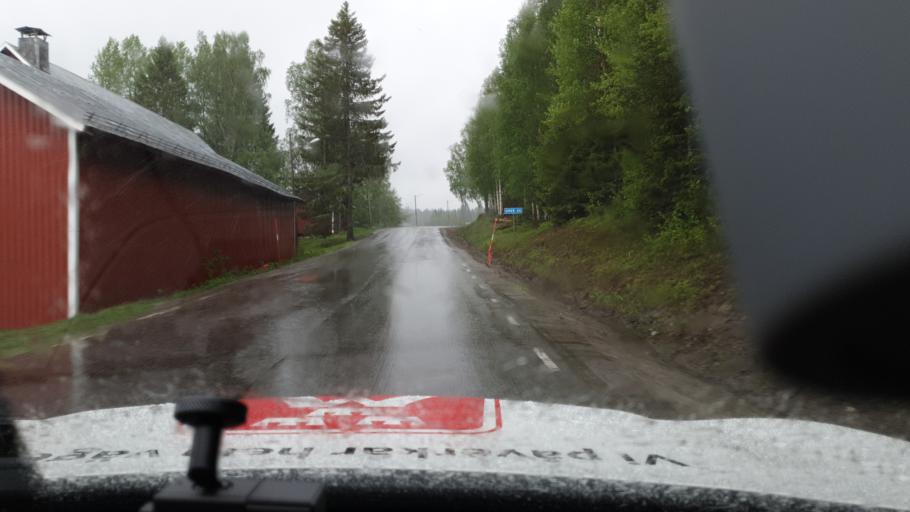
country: SE
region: Vaesterbotten
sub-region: Umea Kommun
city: Roback
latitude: 64.0259
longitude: 20.0872
